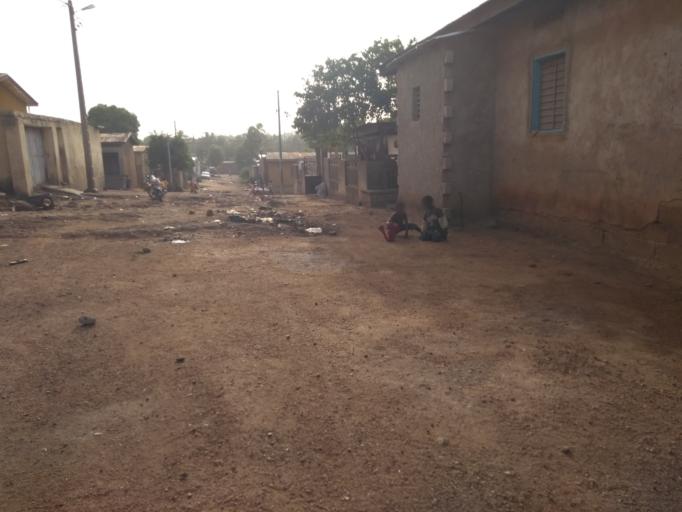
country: CI
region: Vallee du Bandama
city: Bouake
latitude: 7.7080
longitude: -5.0275
